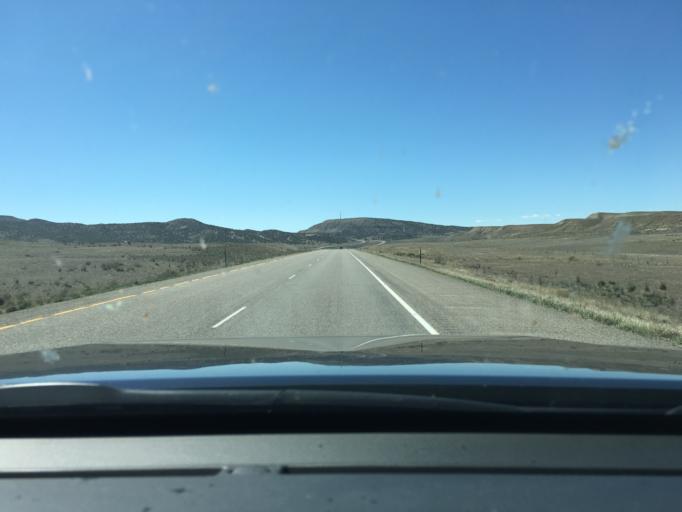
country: US
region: Colorado
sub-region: Mesa County
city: Loma
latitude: 39.2277
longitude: -108.9267
